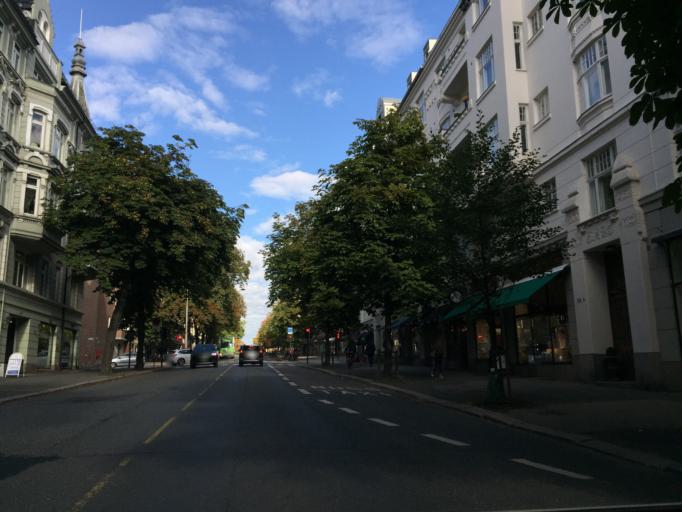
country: NO
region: Oslo
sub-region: Oslo
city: Sjolyststranda
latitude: 59.9164
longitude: 10.7120
